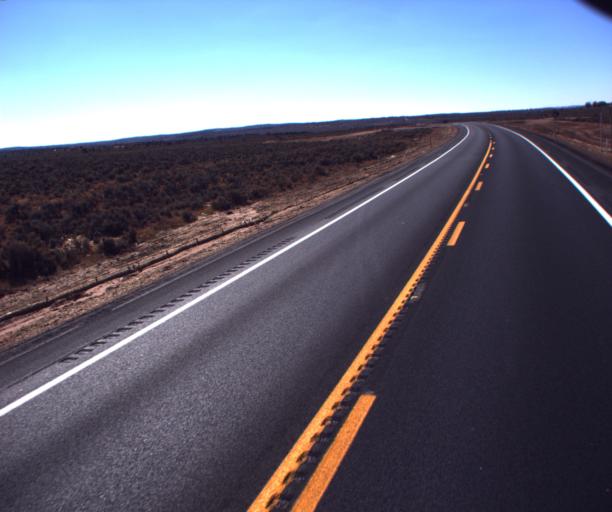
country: US
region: Arizona
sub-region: Apache County
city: Ganado
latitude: 35.7183
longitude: -109.4770
